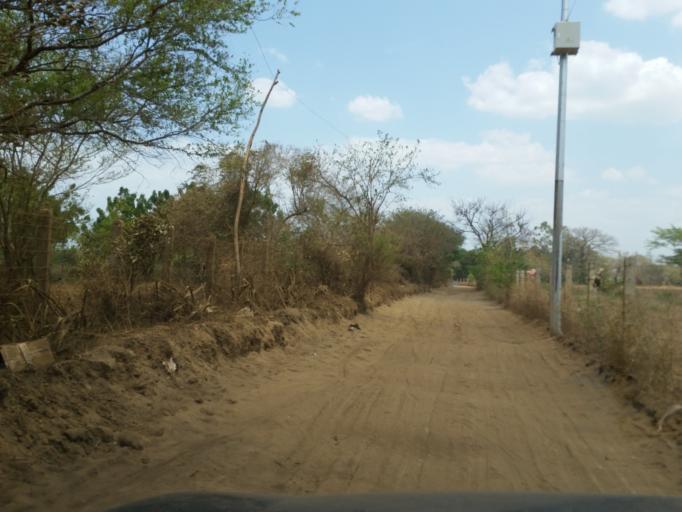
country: NI
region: Managua
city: Managua
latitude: 12.1248
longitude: -86.1631
